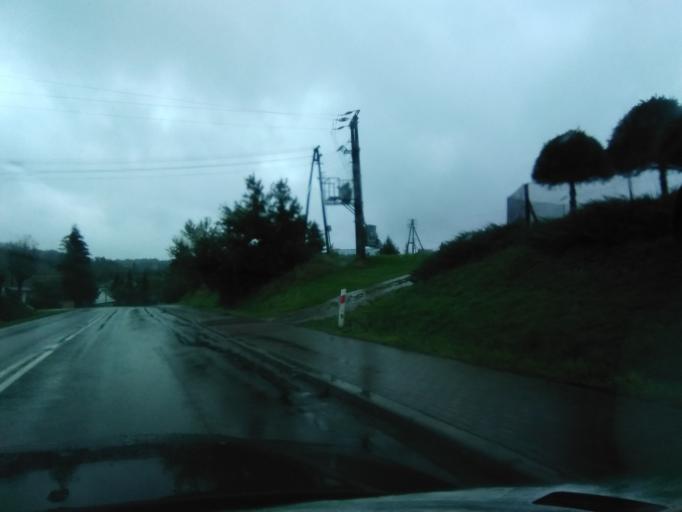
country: PL
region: Subcarpathian Voivodeship
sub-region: Powiat ropczycko-sedziszowski
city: Niedzwiada
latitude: 50.0259
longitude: 21.5466
